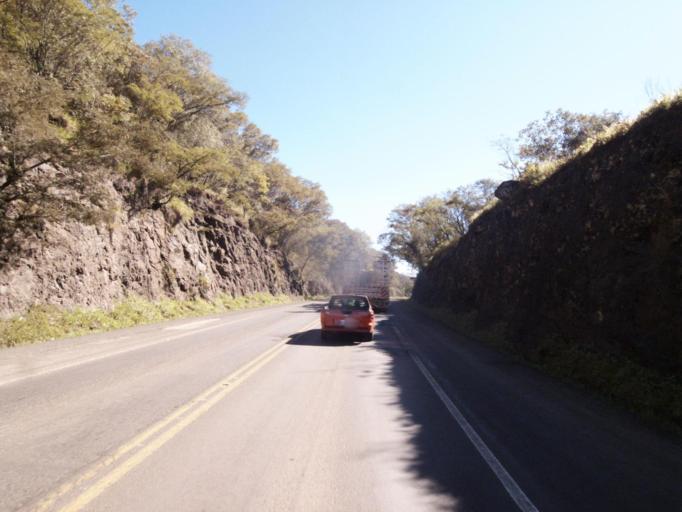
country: AR
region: Misiones
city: Bernardo de Irigoyen
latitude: -26.7697
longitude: -53.4782
